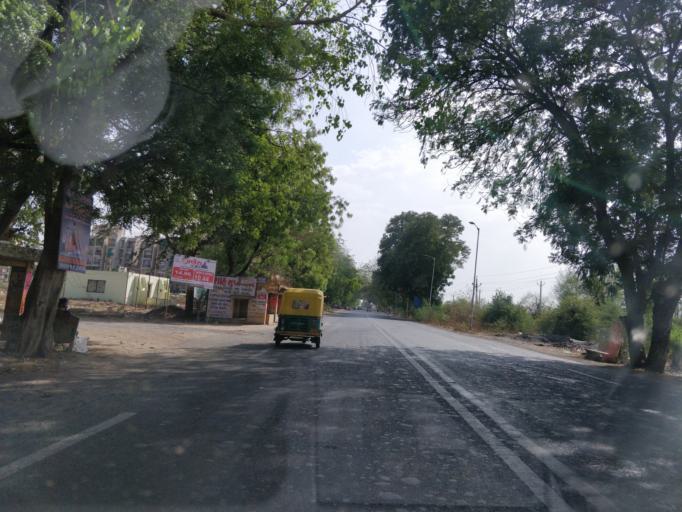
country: IN
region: Gujarat
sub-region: Ahmadabad
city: Naroda
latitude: 23.0852
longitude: 72.6800
